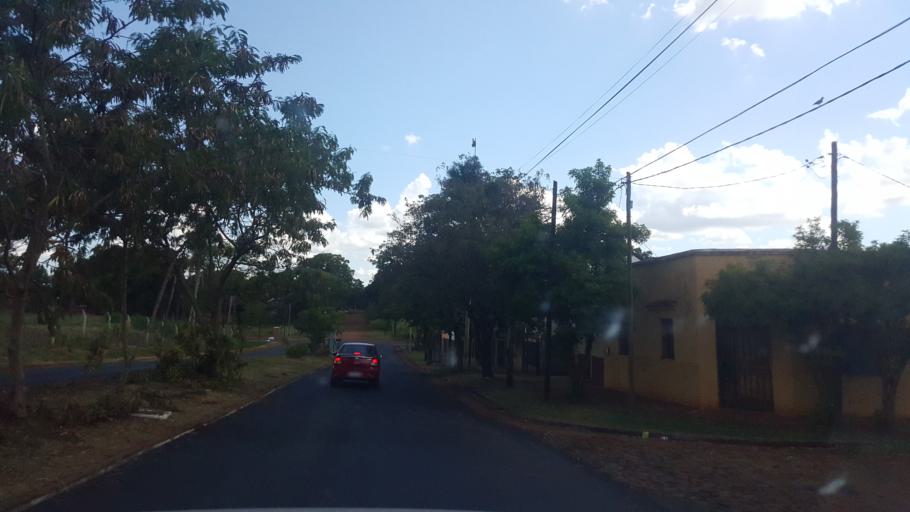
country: AR
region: Misiones
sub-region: Departamento de Capital
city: Posadas
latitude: -27.3607
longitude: -55.9195
